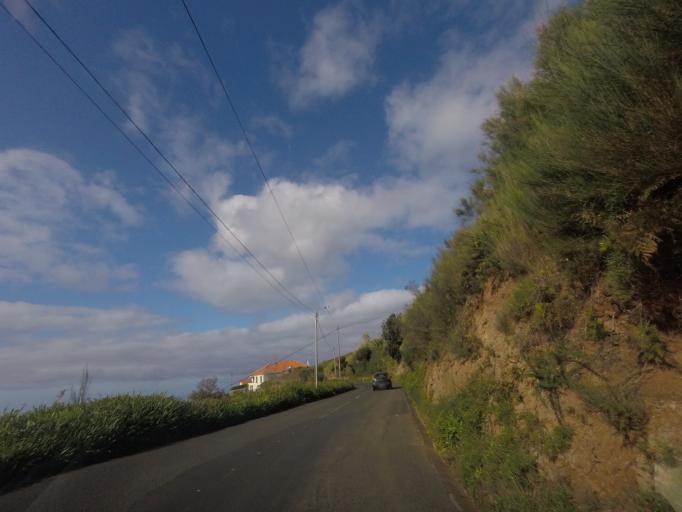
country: PT
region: Madeira
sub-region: Calheta
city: Faja da Ovelha
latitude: 32.8041
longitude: -17.2421
